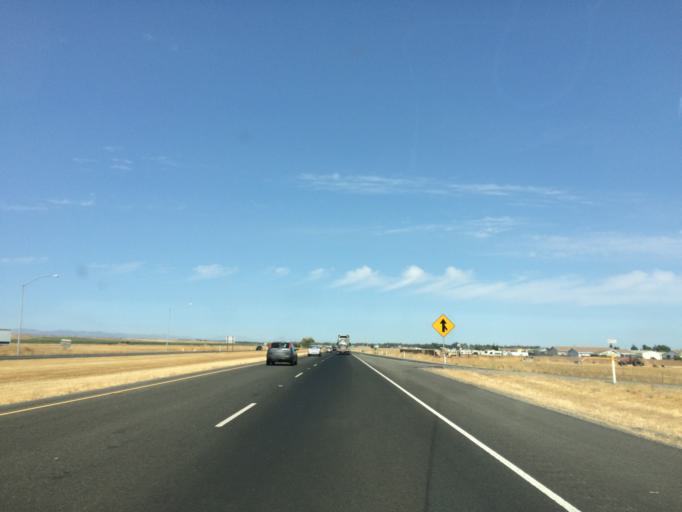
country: US
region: California
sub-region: Yolo County
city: Dunnigan
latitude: 38.8623
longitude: -121.9546
